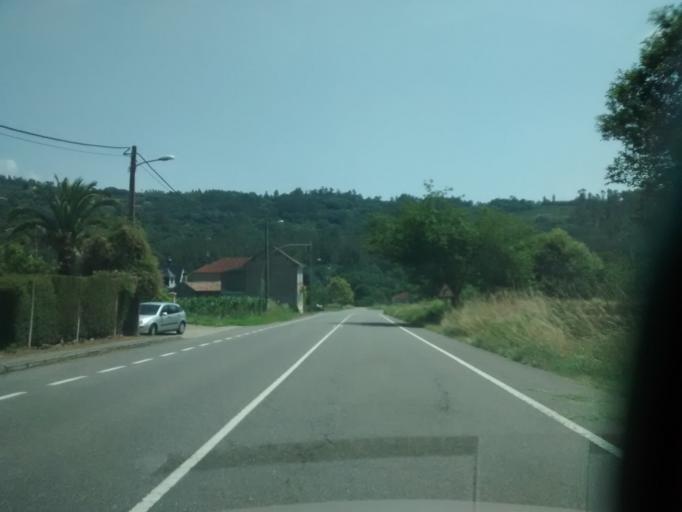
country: ES
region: Galicia
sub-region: Provincia de Ourense
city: Boboras
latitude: 42.4509
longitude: -8.1445
